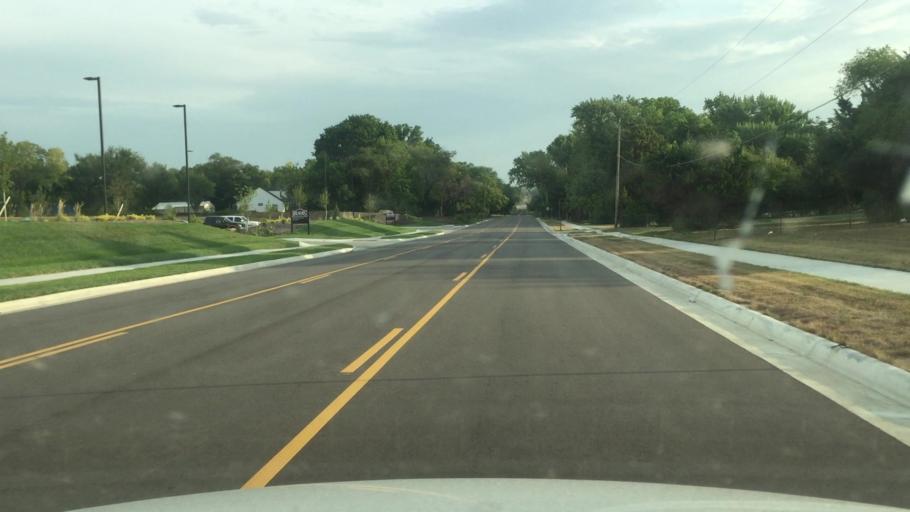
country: US
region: Kansas
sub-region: Shawnee County
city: Topeka
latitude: 39.0463
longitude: -95.6134
